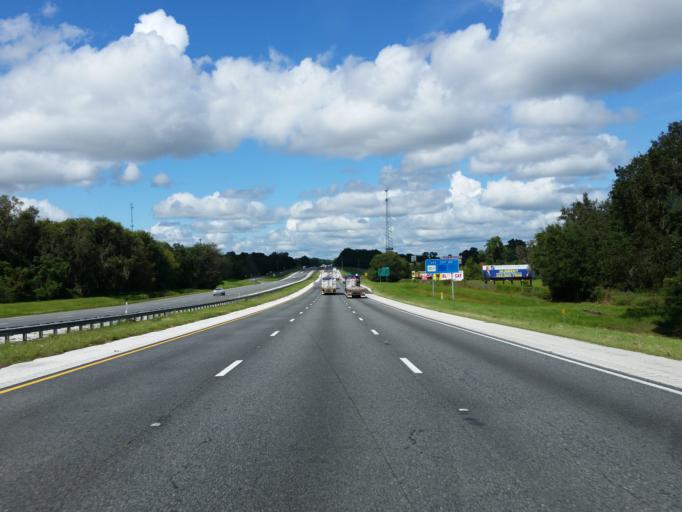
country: US
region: Florida
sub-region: Marion County
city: Citra
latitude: 29.4012
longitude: -82.2433
